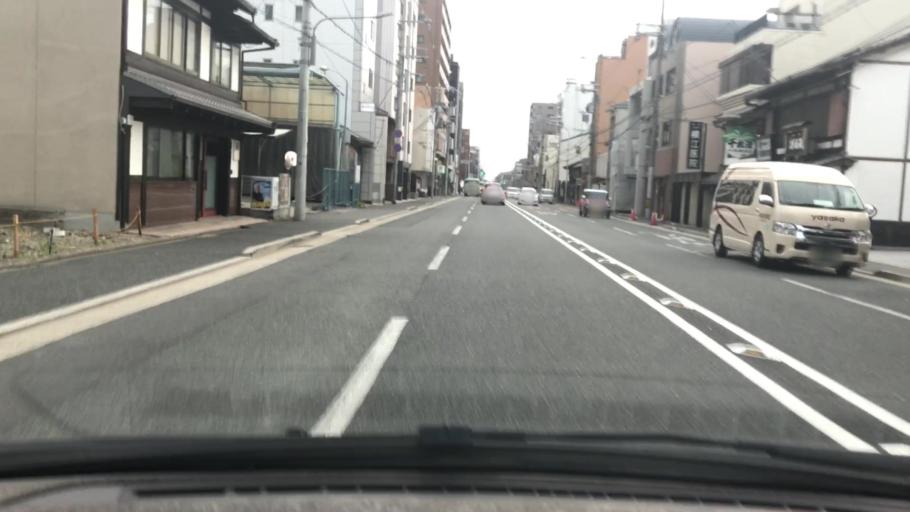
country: JP
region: Kyoto
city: Kyoto
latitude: 34.9983
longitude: 135.7492
